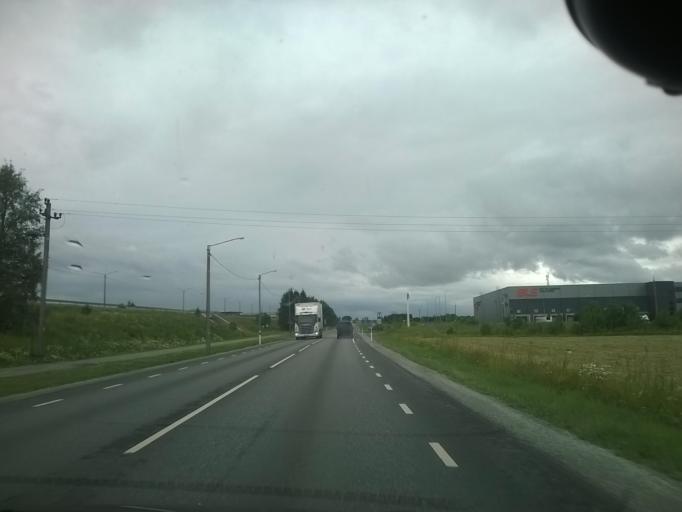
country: EE
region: Harju
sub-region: Rae vald
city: Jueri
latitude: 59.3776
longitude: 24.8461
